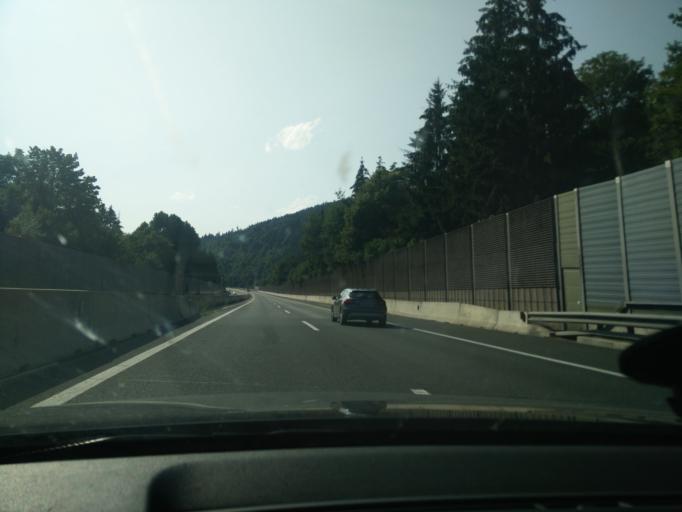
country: AT
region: Carinthia
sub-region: Politischer Bezirk Klagenfurt Land
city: Maria Worth
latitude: 46.6372
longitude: 14.1593
